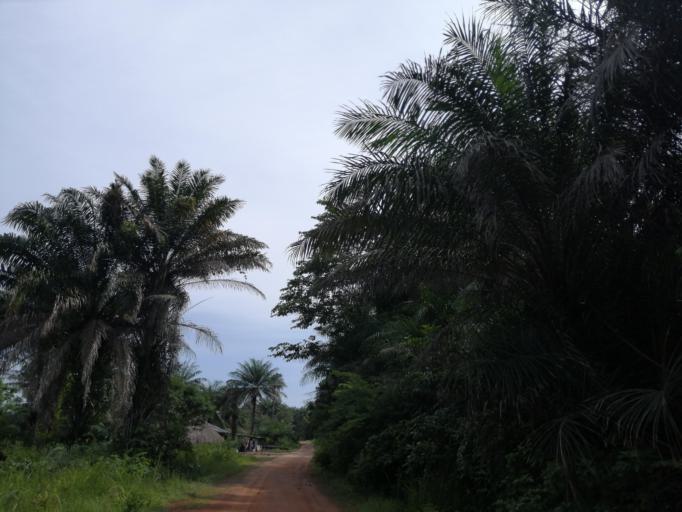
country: SL
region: Northern Province
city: Mange
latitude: 8.8037
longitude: -12.9267
